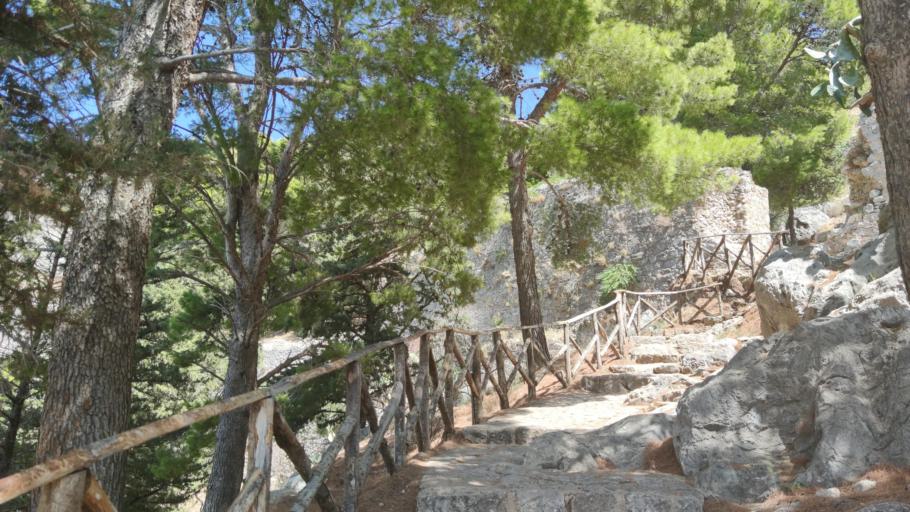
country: IT
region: Sicily
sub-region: Palermo
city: Cefalu
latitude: 38.0368
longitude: 14.0244
